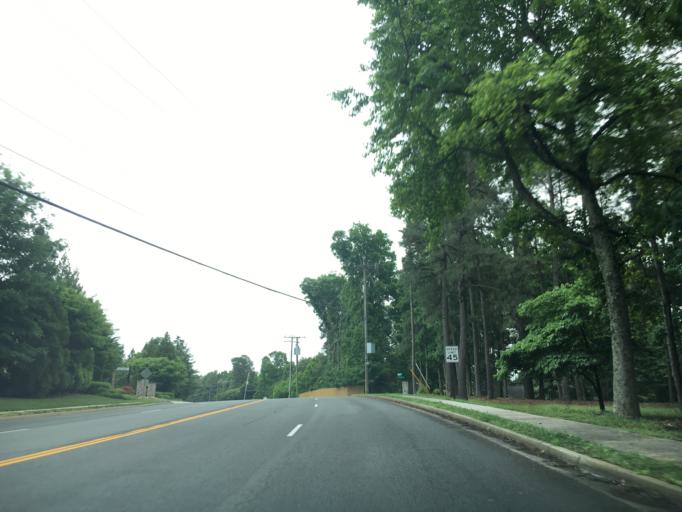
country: US
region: Virginia
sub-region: Henrico County
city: Short Pump
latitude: 37.6327
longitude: -77.6248
